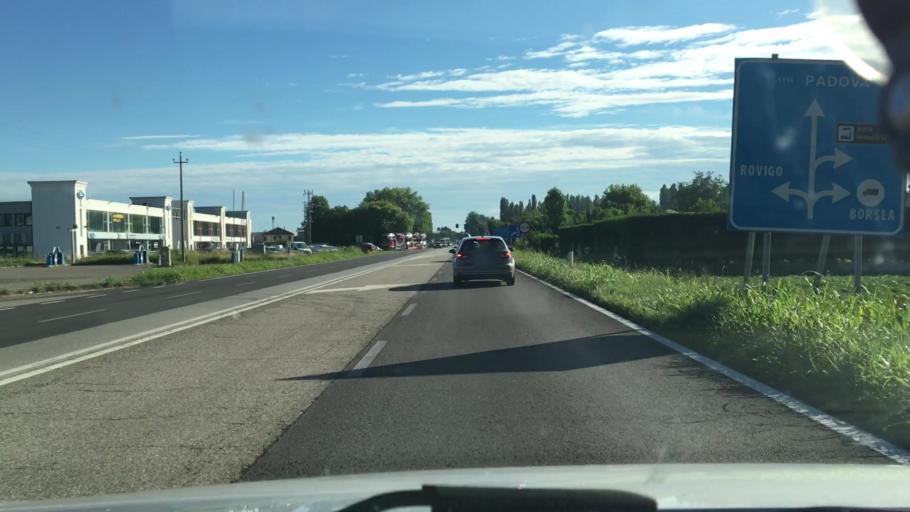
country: IT
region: Veneto
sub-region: Provincia di Rovigo
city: Rovigo
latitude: 45.0423
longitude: 11.7848
